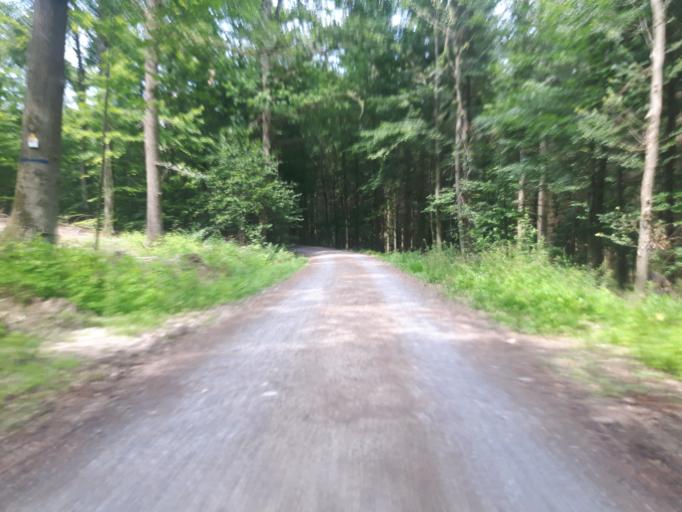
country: DE
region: Baden-Wuerttemberg
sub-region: Regierungsbezirk Stuttgart
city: Cleebronn
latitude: 49.0314
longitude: 9.0085
